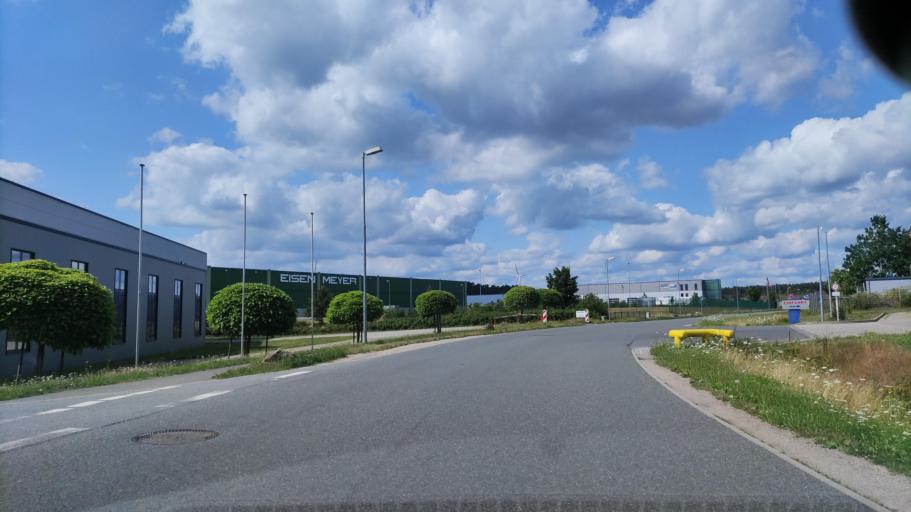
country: DE
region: Lower Saxony
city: Soltau
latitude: 52.9977
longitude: 9.9199
